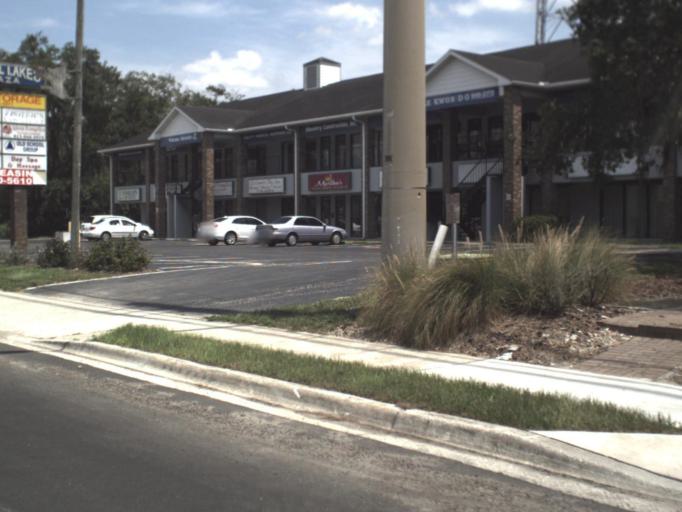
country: US
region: Florida
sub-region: Hillsborough County
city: Lutz
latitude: 28.1368
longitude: -82.4630
